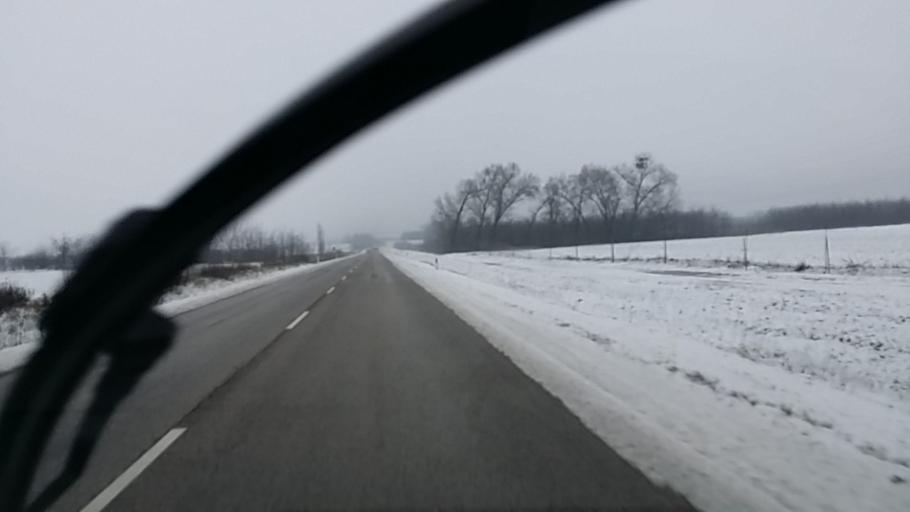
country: HU
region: Komarom-Esztergom
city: Komarom
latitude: 47.7242
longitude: 18.1073
